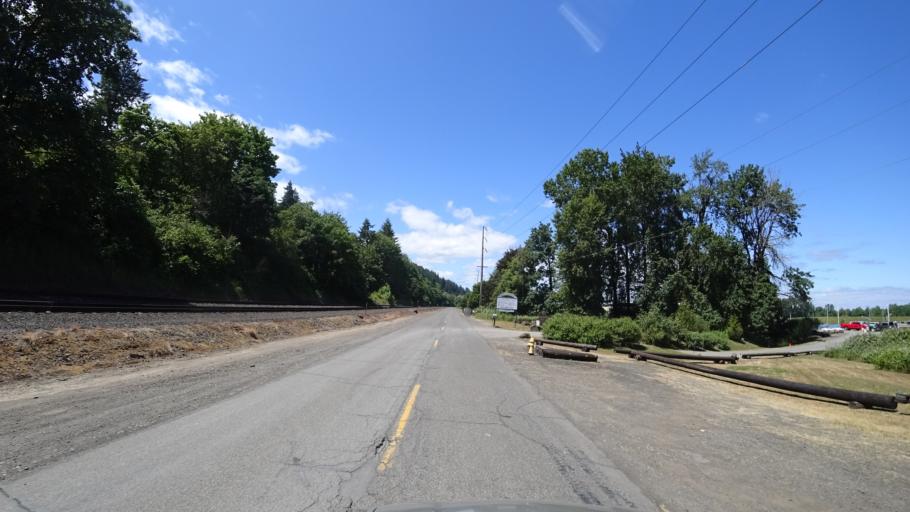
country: US
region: Oregon
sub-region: Washington County
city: Oak Hills
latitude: 45.6175
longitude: -122.8052
